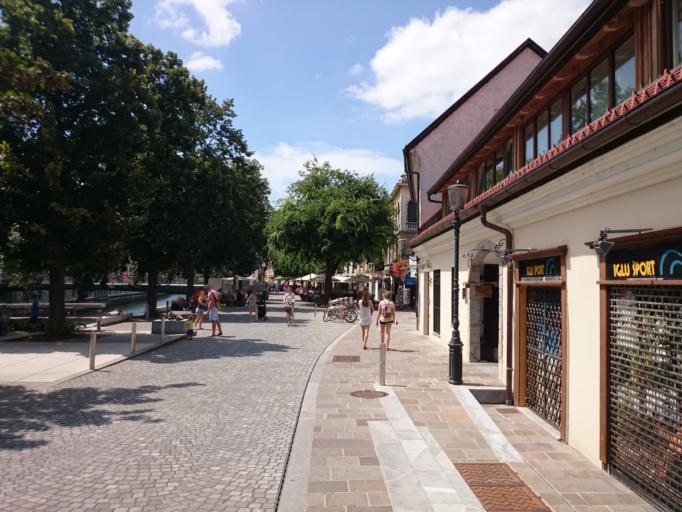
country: SI
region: Ljubljana
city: Ljubljana
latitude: 46.0521
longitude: 14.5097
